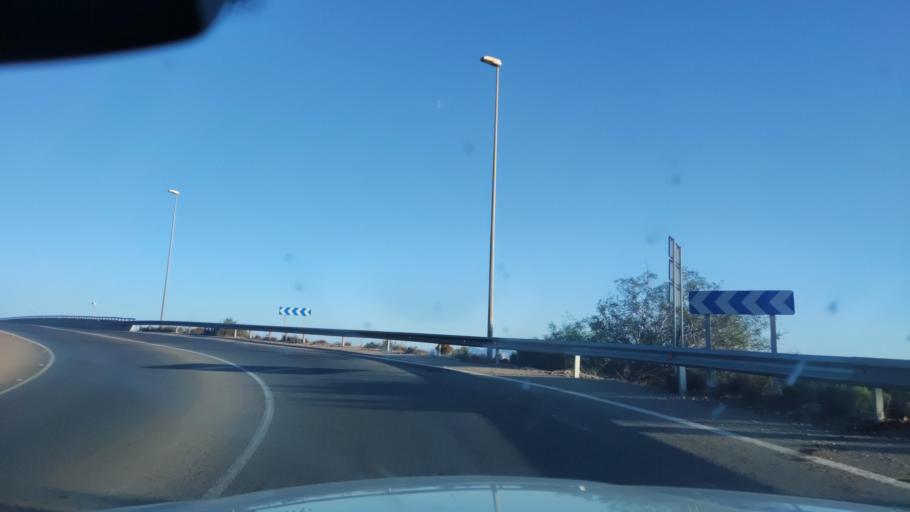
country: ES
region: Murcia
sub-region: Murcia
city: Los Alcazares
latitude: 37.7694
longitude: -0.8461
